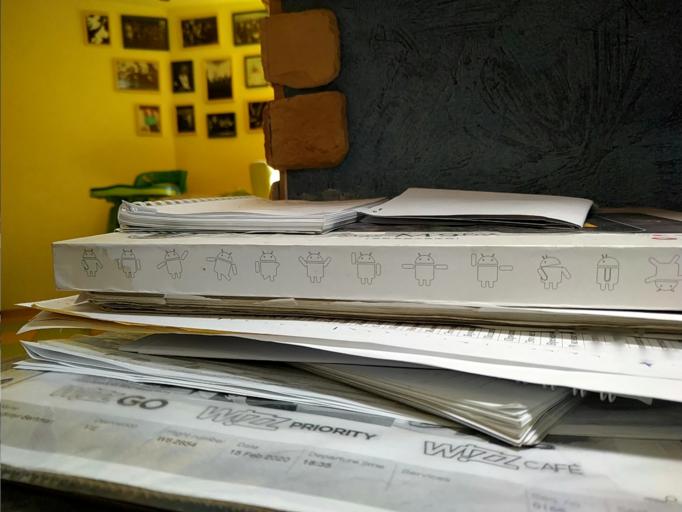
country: RU
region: Novgorod
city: Sol'tsy
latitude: 57.9398
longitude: 30.3338
